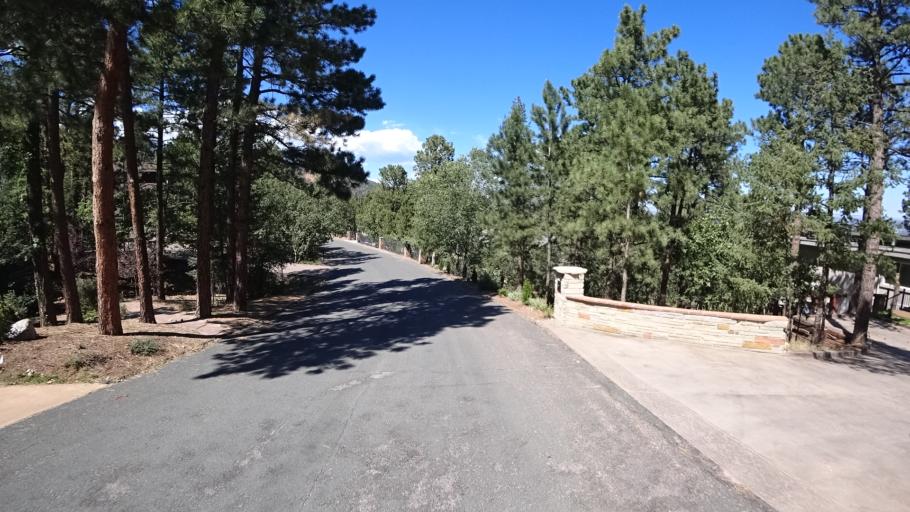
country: US
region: Colorado
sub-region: El Paso County
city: Colorado Springs
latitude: 38.7818
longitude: -104.8617
